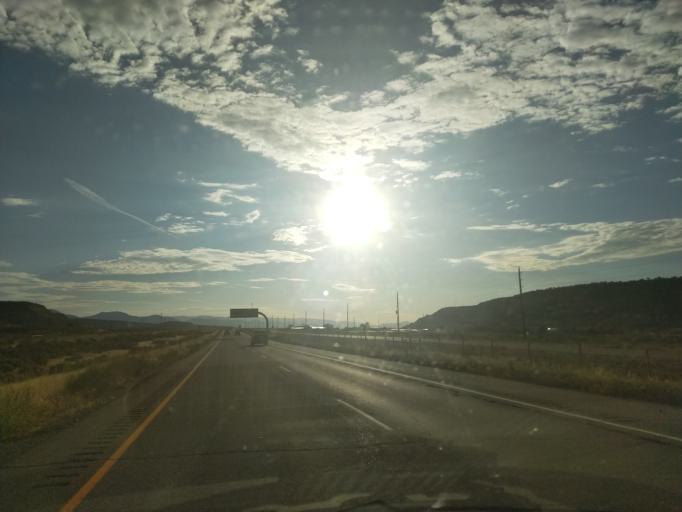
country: US
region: Colorado
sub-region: Garfield County
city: Rifle
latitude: 39.5159
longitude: -107.8596
